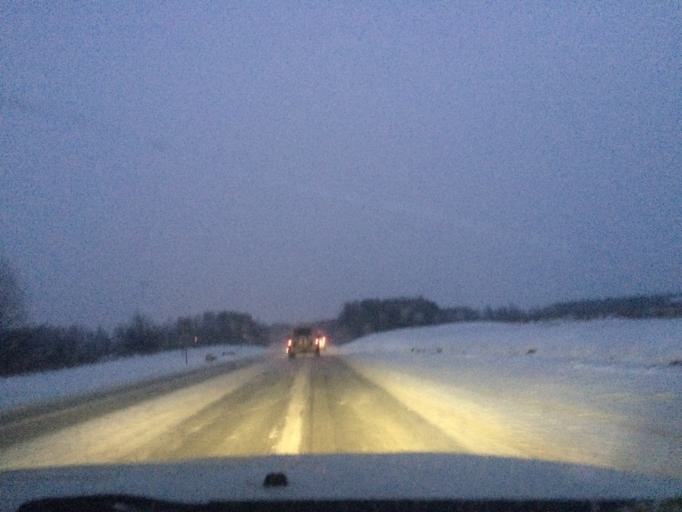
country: RU
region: Tula
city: Barsuki
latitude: 54.1706
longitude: 37.4587
